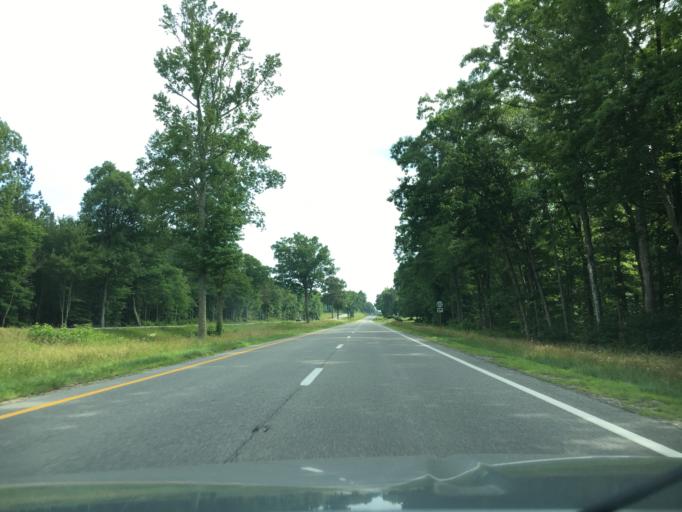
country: US
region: Virginia
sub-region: Mecklenburg County
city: Chase City
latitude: 36.9639
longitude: -78.4946
